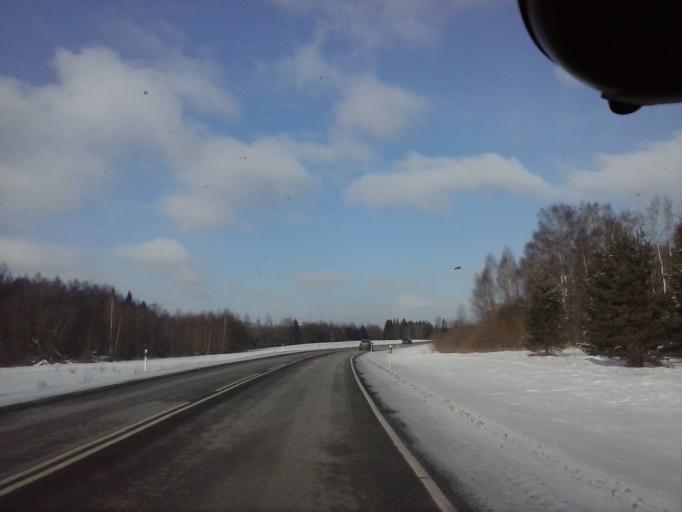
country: EE
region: Viljandimaa
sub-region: Viljandi linn
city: Viljandi
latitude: 58.3430
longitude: 25.4663
